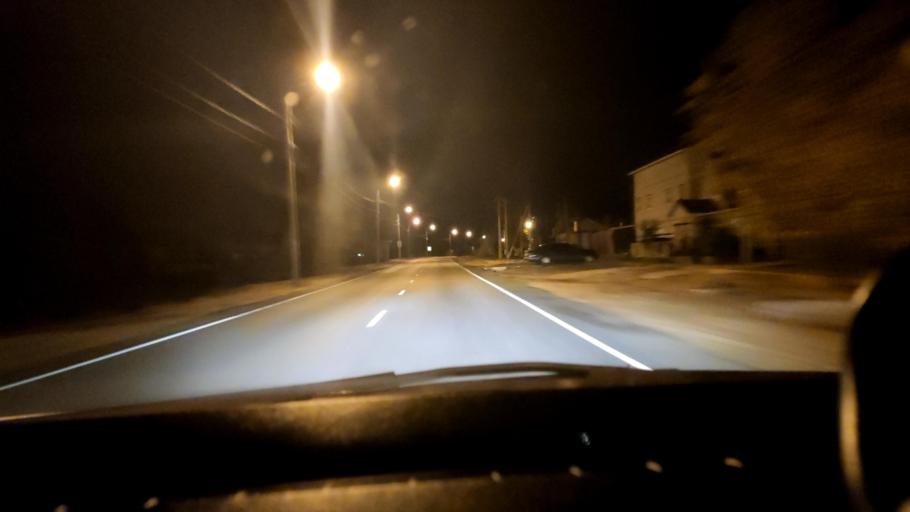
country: RU
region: Voronezj
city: Shilovo
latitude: 51.5652
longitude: 39.0509
